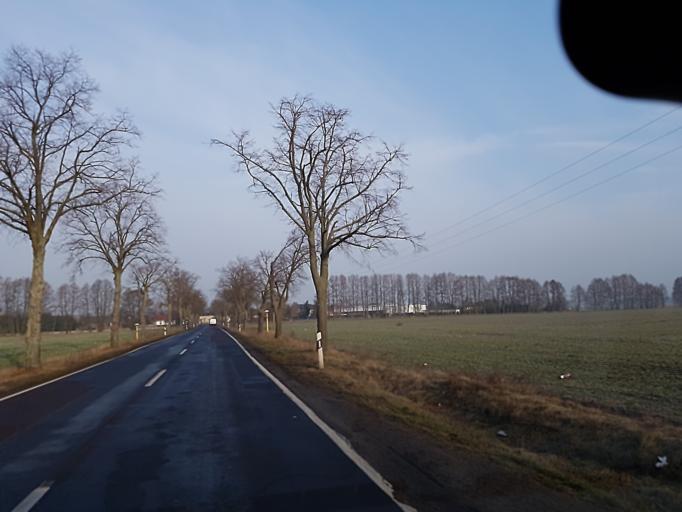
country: DE
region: Brandenburg
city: Wenzlow
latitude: 52.2945
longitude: 12.4587
